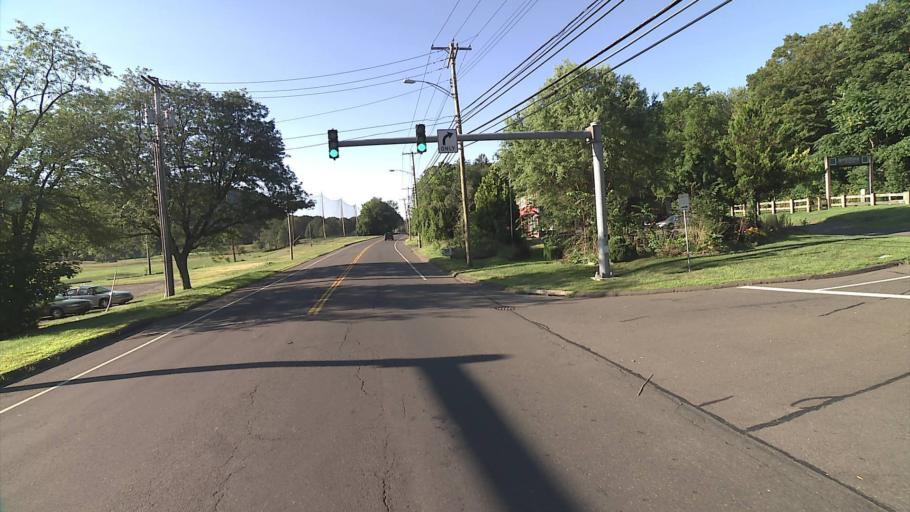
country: US
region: Connecticut
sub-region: New Haven County
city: Hamden
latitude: 41.4369
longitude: -72.9089
